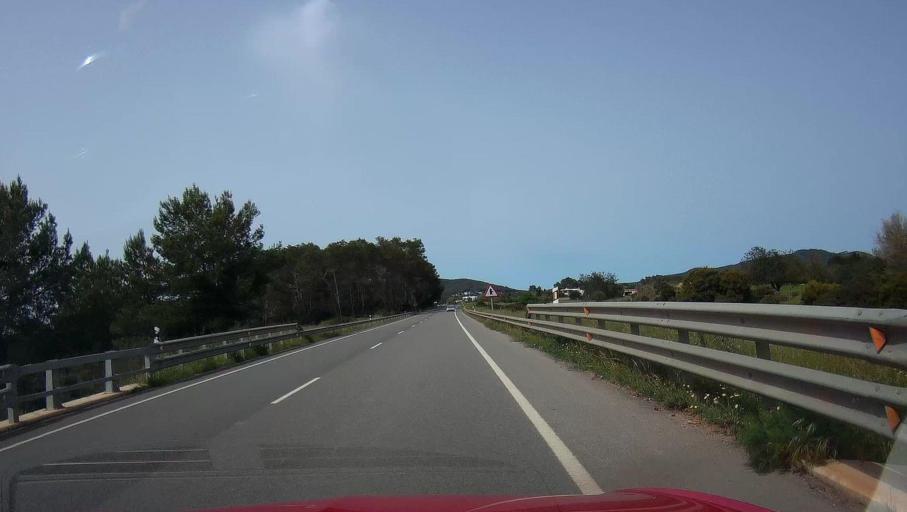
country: ES
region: Balearic Islands
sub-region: Illes Balears
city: Santa Eularia des Riu
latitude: 39.0143
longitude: 1.4877
